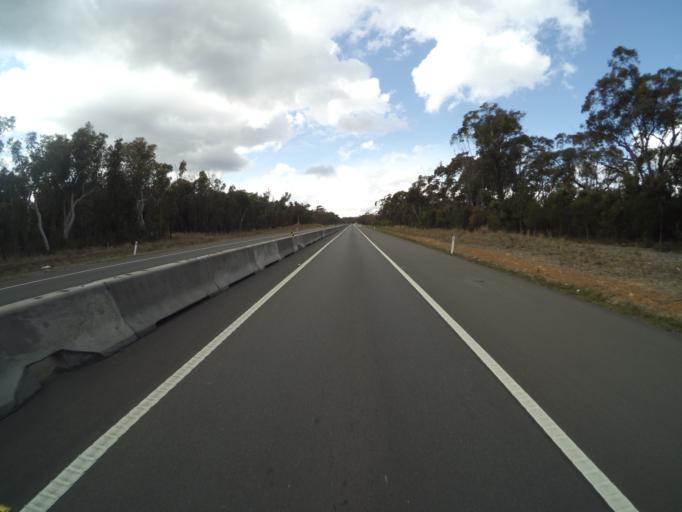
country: AU
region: New South Wales
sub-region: Wollongong
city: Mount Keira
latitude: -34.3372
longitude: 150.7875
